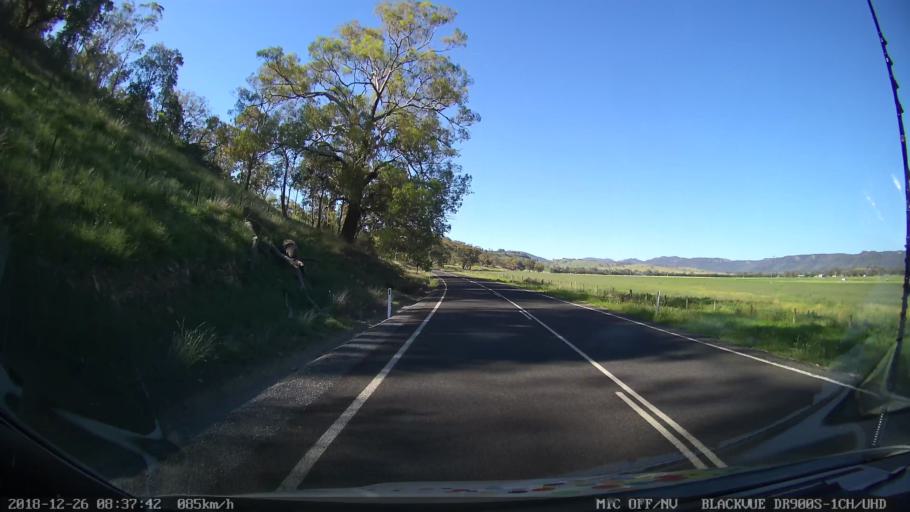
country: AU
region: New South Wales
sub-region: Upper Hunter Shire
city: Merriwa
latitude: -32.4349
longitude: 150.0876
